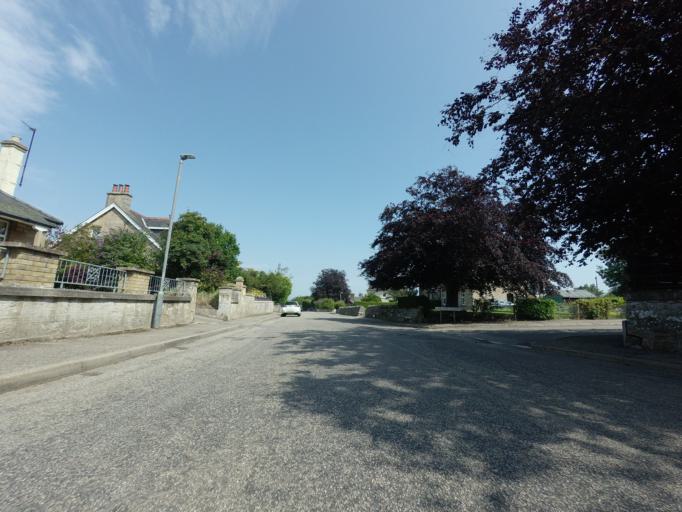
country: GB
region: Scotland
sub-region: Highland
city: Tain
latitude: 57.8082
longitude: -4.0552
